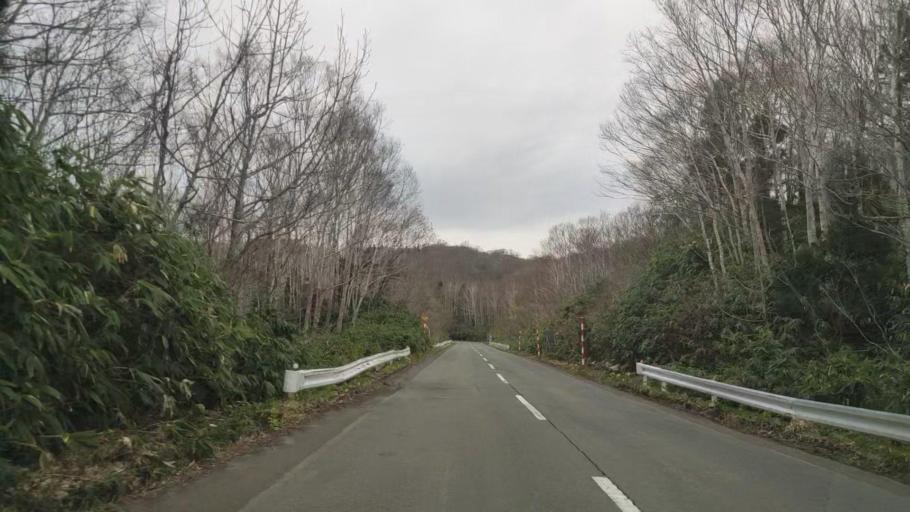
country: JP
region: Akita
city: Hanawa
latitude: 40.4149
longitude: 140.8463
